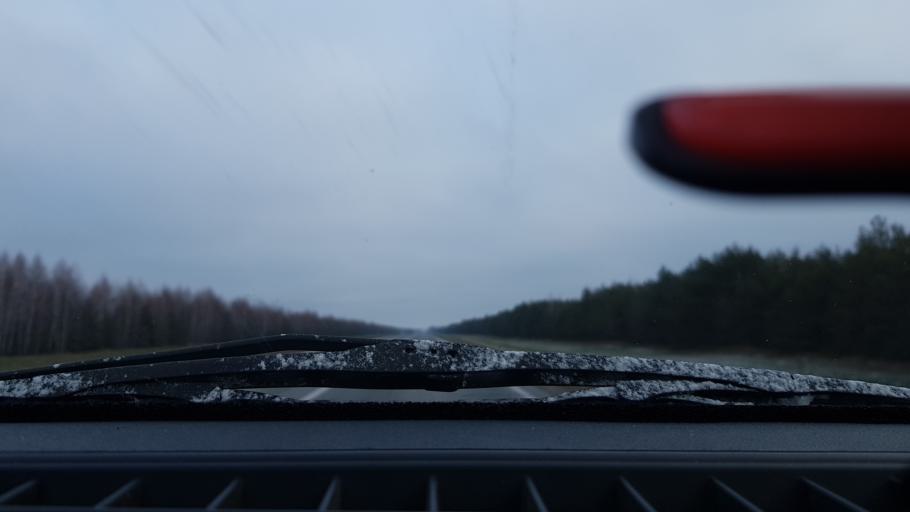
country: RU
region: Tatarstan
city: Kuybyshevskiy Zaton
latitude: 54.9558
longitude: 49.4772
